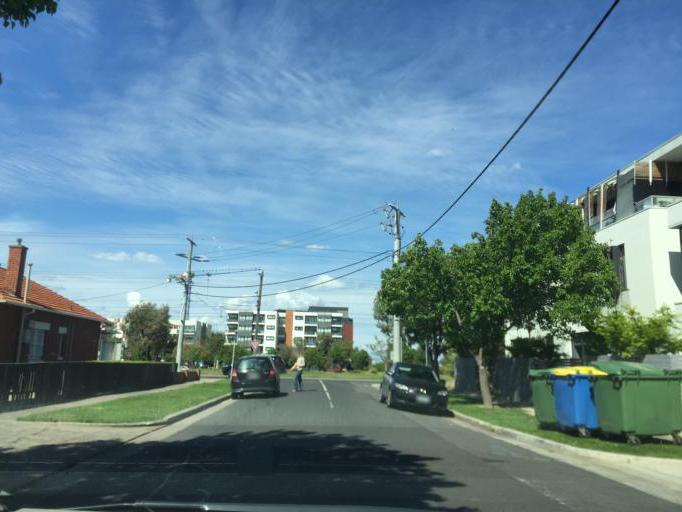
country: AU
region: Victoria
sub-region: Maribyrnong
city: Maribyrnong
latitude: -37.7827
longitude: 144.8905
